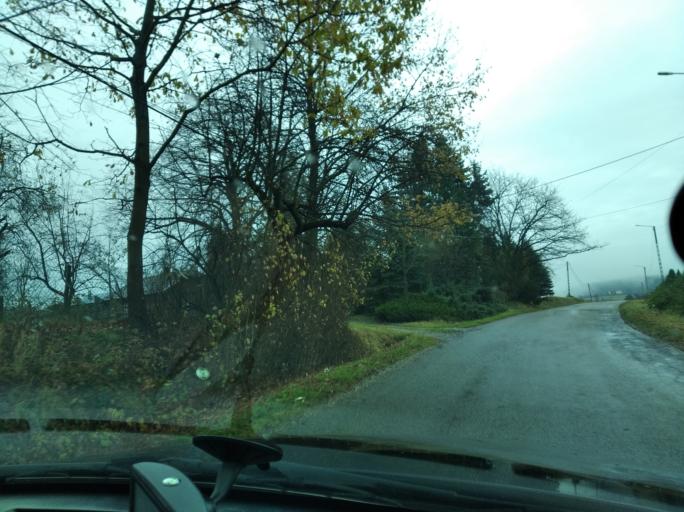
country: PL
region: Subcarpathian Voivodeship
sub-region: Powiat strzyzowski
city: Babica
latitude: 49.9288
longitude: 21.8765
